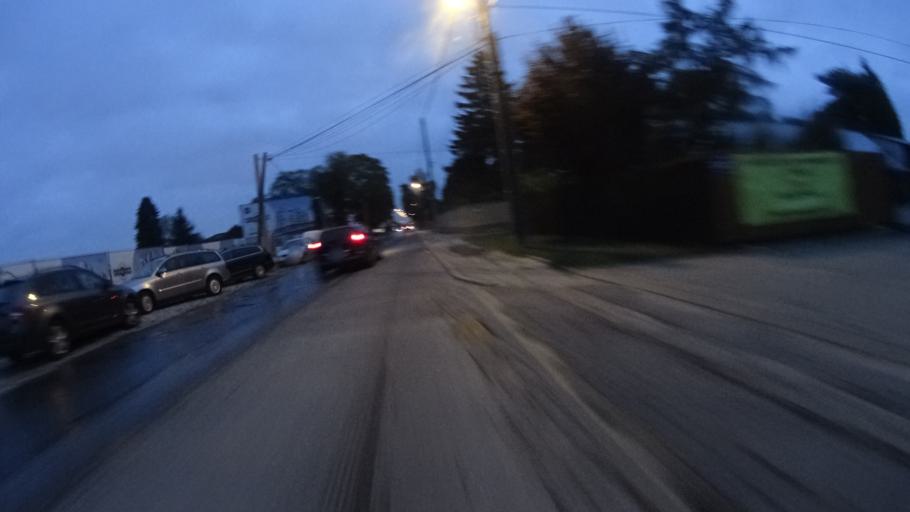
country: PL
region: Masovian Voivodeship
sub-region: Warszawa
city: Ursus
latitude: 52.2276
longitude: 20.8849
